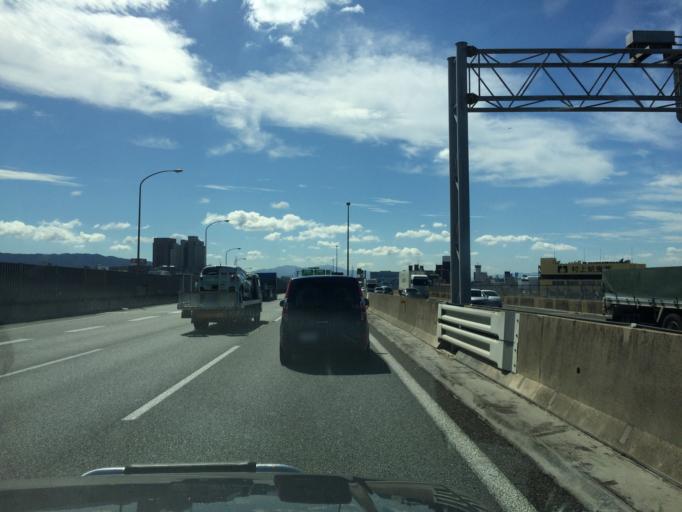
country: JP
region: Osaka
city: Daitocho
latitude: 34.6896
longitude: 135.5934
